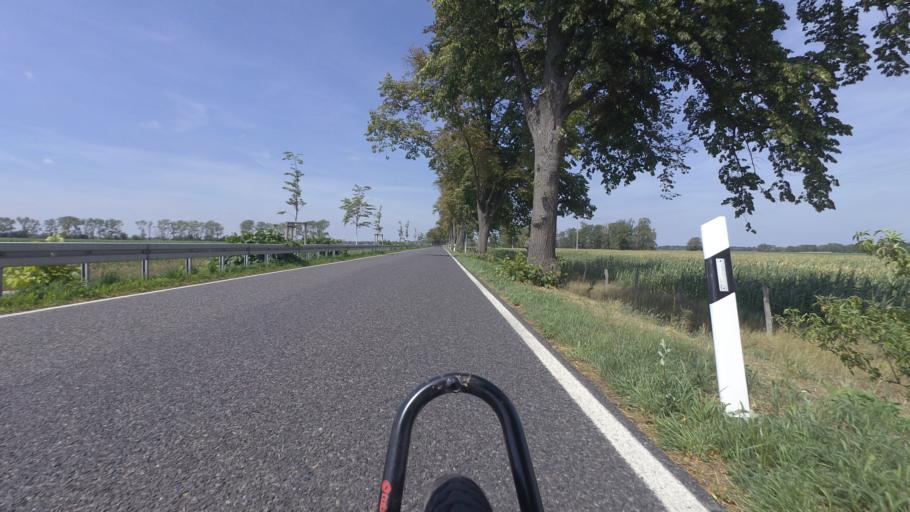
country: DE
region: Brandenburg
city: Rhinow
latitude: 52.7645
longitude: 12.2856
